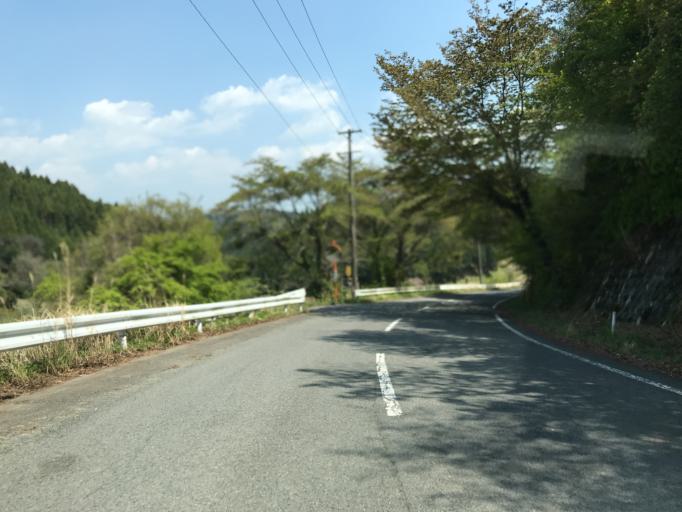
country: JP
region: Ibaraki
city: Kitaibaraki
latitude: 36.9610
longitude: 140.6952
